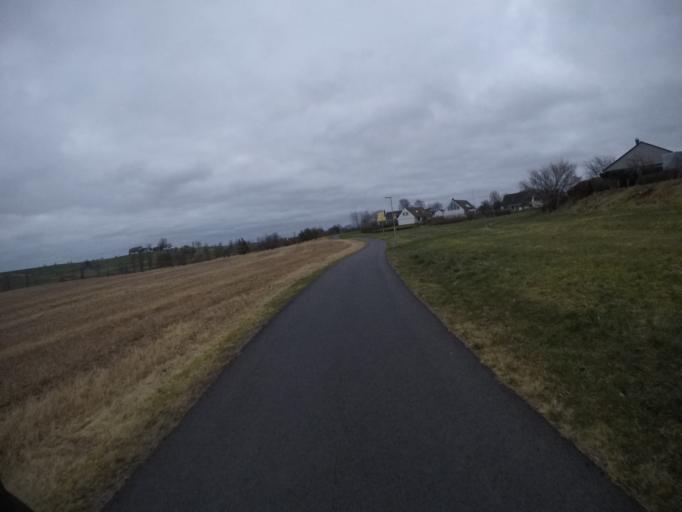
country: SE
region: Halland
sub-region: Laholms Kommun
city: Laholm
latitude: 56.5105
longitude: 13.0242
